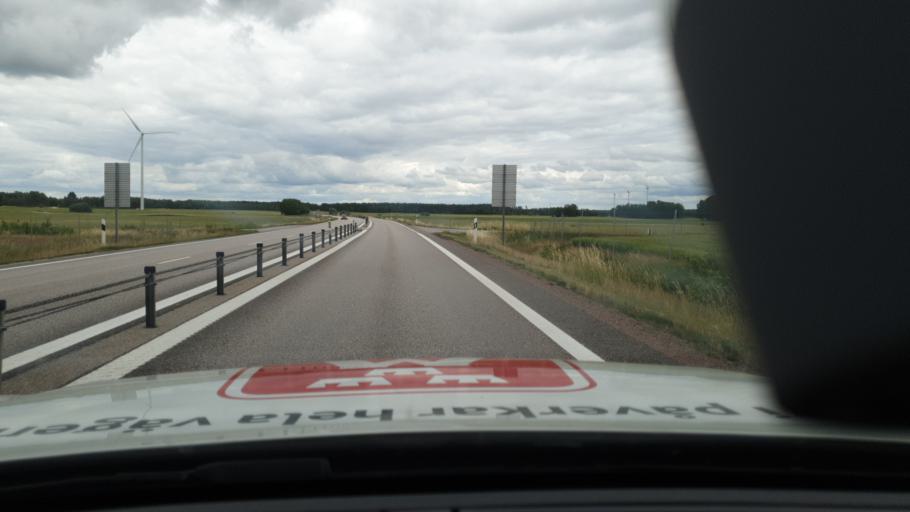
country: SE
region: Vaestra Goetaland
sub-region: Vara Kommun
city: Kvanum
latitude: 58.3454
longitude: 13.2216
